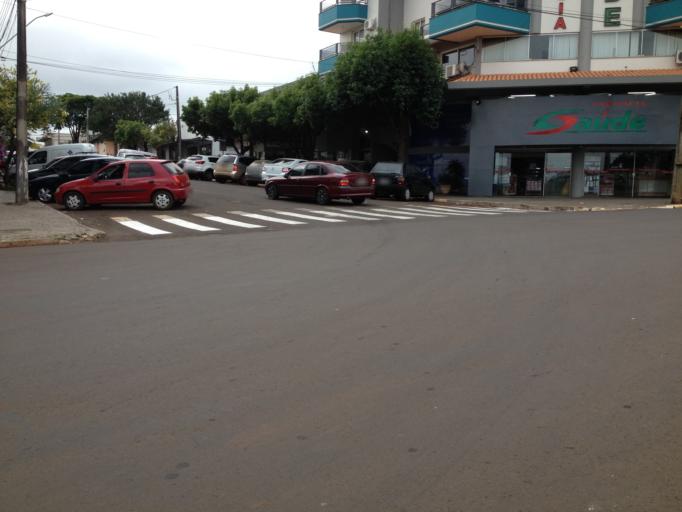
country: BR
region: Parana
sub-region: Matelandia
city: Matelandia
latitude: -25.2425
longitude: -53.9772
